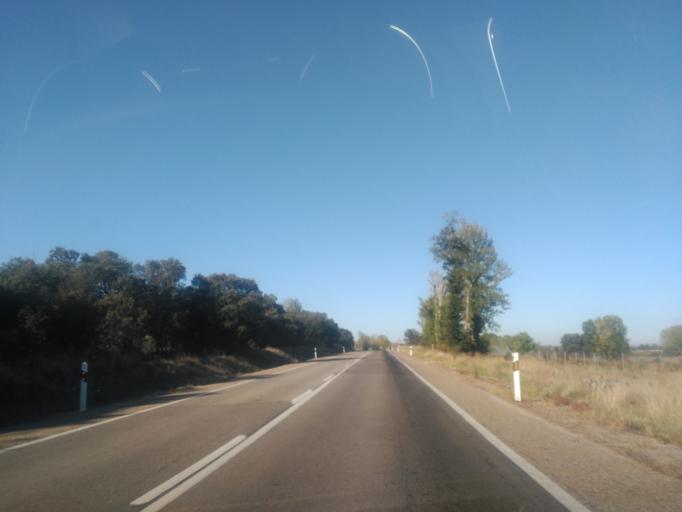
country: ES
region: Castille and Leon
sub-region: Provincia de Burgos
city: Castrillo de la Vega
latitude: 41.6604
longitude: -3.7601
